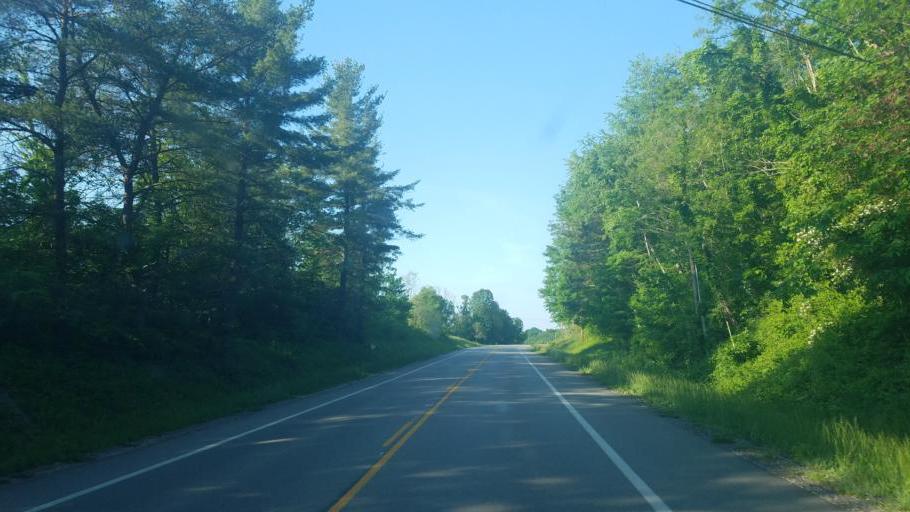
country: US
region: West Virginia
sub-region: Mason County
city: New Haven
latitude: 39.1428
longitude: -81.8547
